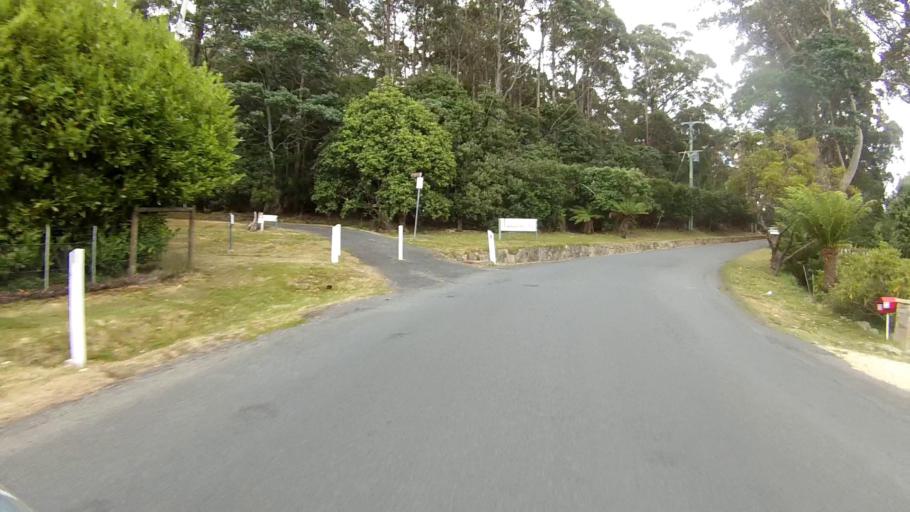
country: AU
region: Tasmania
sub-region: Hobart
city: Dynnyrne
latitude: -42.9177
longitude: 147.2614
